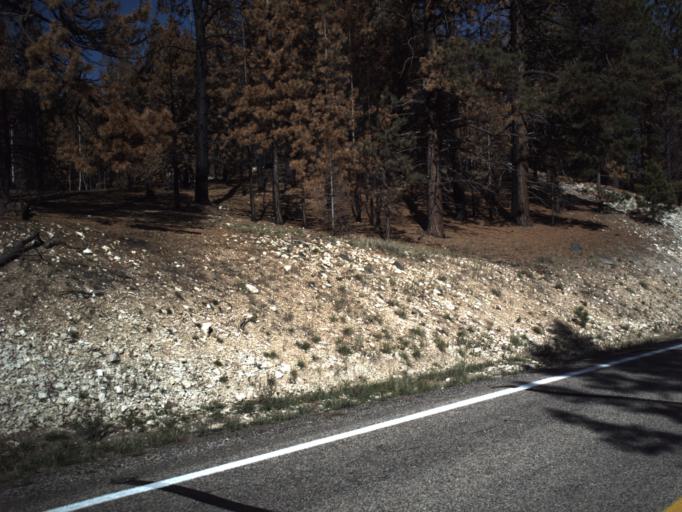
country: US
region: Utah
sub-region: Iron County
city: Parowan
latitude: 37.6549
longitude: -112.6835
